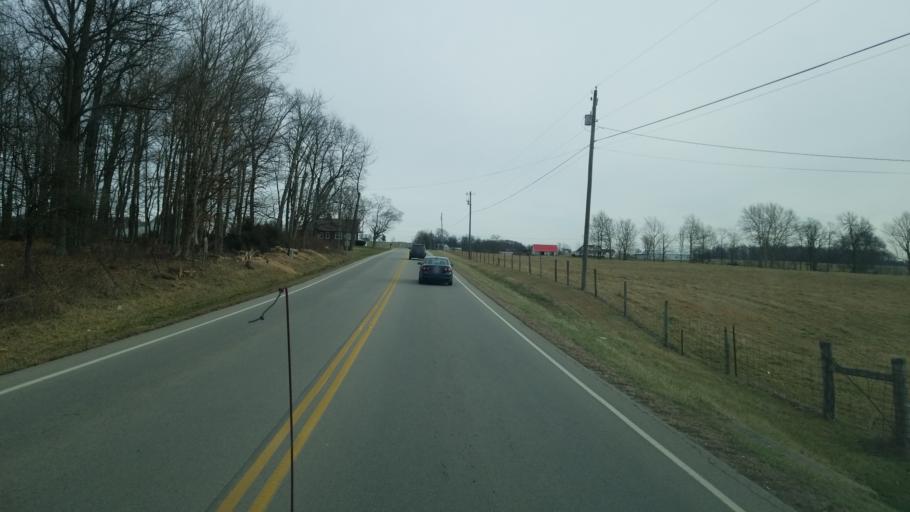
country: US
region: Ohio
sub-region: Adams County
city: Winchester
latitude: 39.0653
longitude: -83.6980
